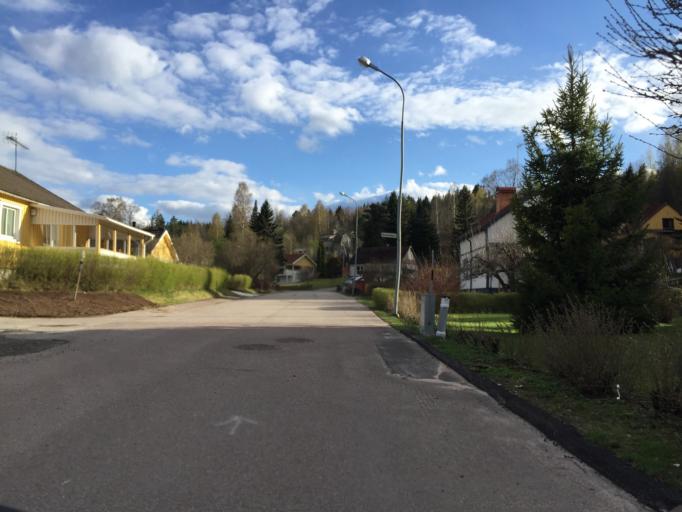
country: SE
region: Dalarna
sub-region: Ludvika Kommun
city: Ludvika
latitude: 60.1334
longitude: 15.1593
